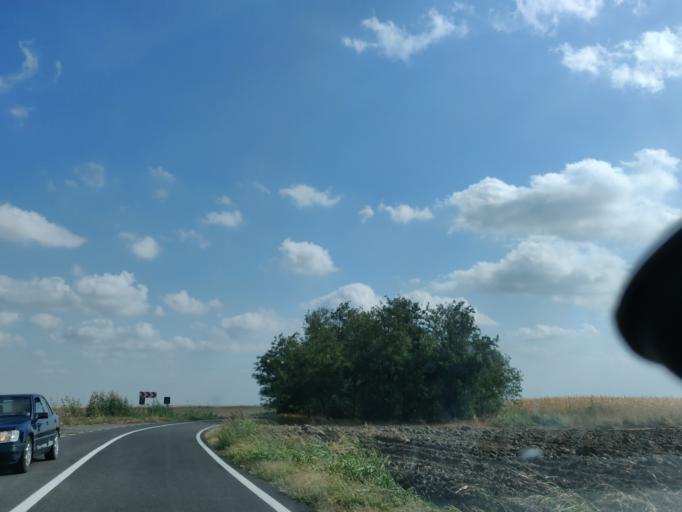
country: RO
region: Vrancea
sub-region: Comuna Ciorasti
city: Mihalceni
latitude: 45.4496
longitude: 27.3622
